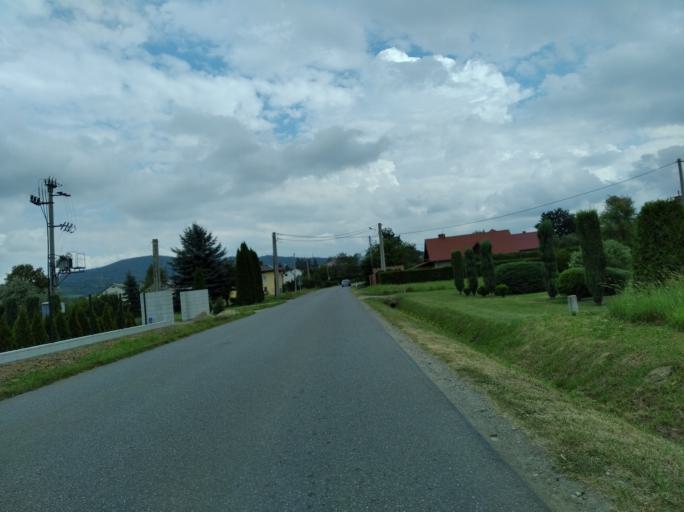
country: PL
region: Subcarpathian Voivodeship
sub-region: Powiat krosnienski
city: Odrzykon
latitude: 49.7401
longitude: 21.7329
